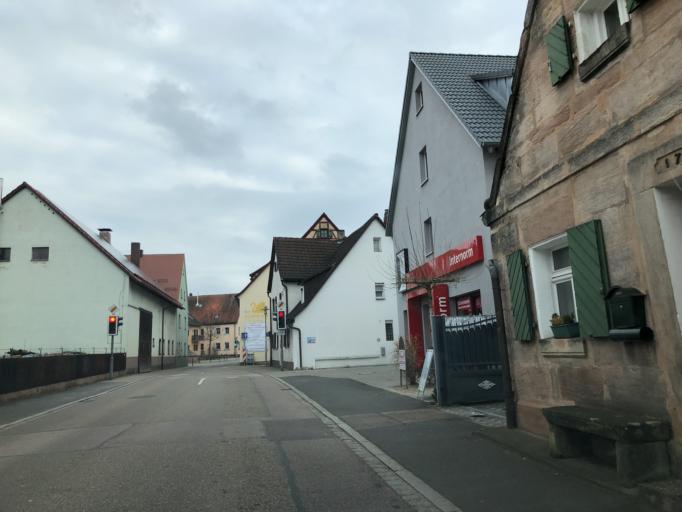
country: DE
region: Bavaria
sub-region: Regierungsbezirk Mittelfranken
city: Rednitzhembach
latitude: 49.2970
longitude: 11.1202
